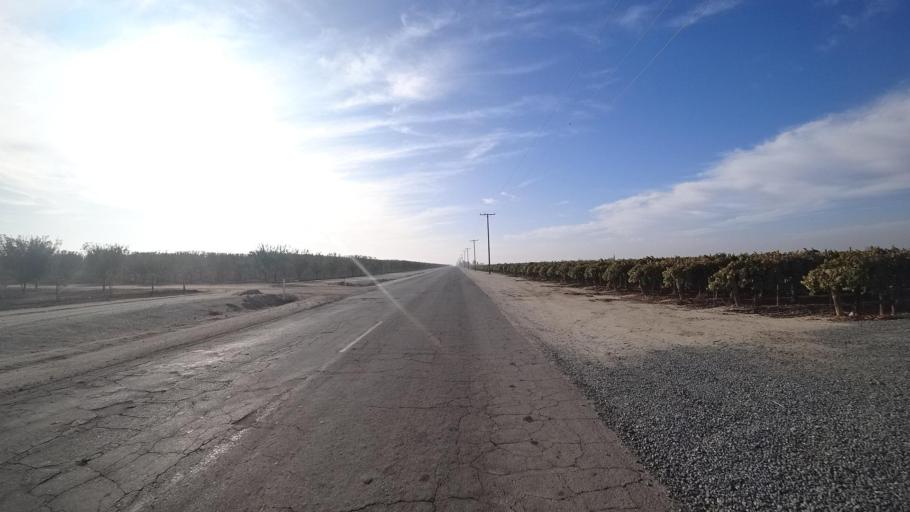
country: US
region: California
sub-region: Kern County
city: McFarland
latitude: 35.6984
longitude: -119.2049
